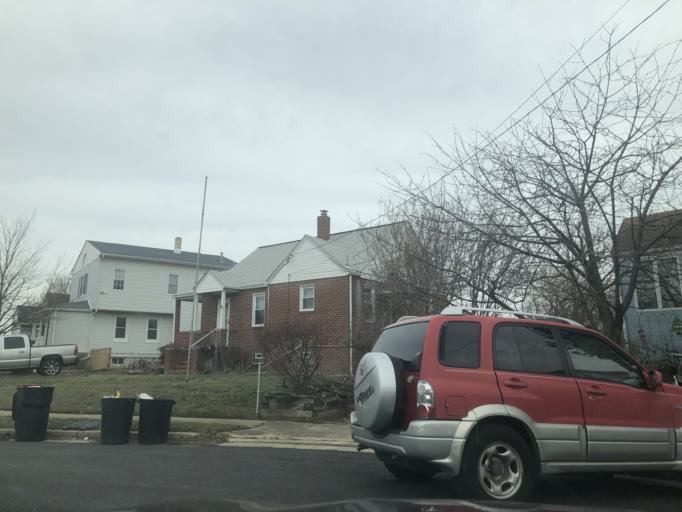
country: US
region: Maryland
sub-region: Baltimore County
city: Dundalk
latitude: 39.2614
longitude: -76.4853
